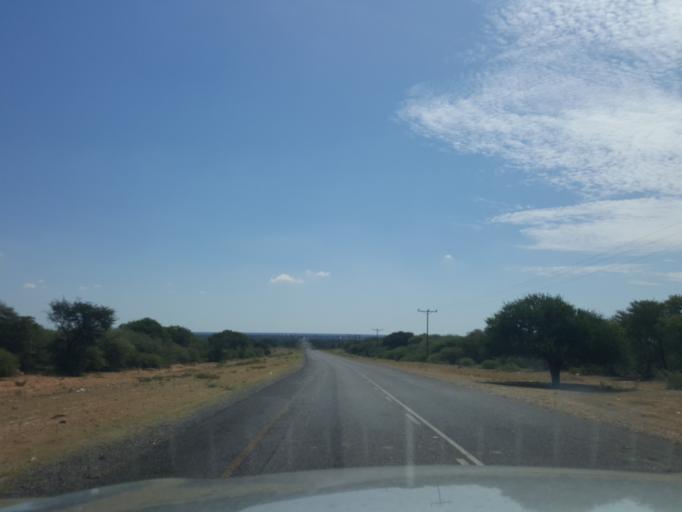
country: BW
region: Kweneng
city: Letlhakeng
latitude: -24.1215
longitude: 25.0831
